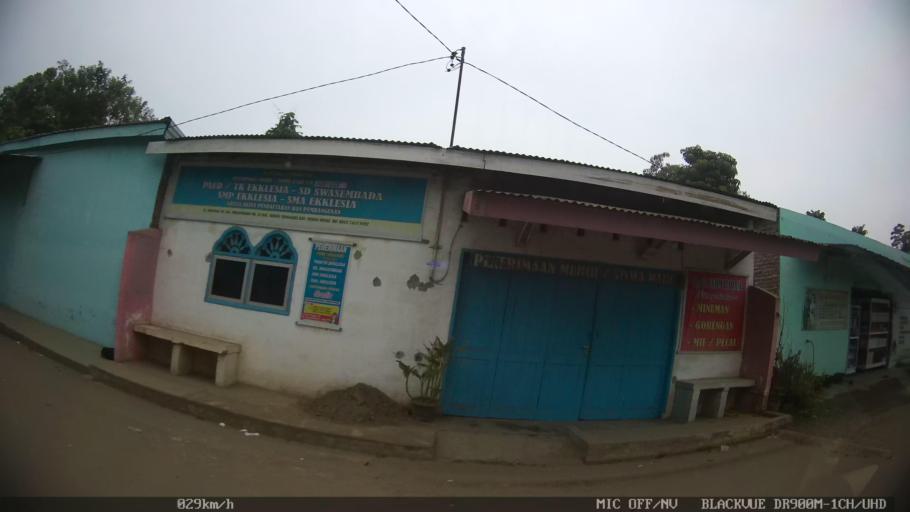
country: ID
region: North Sumatra
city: Deli Tua
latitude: 3.5515
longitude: 98.7280
